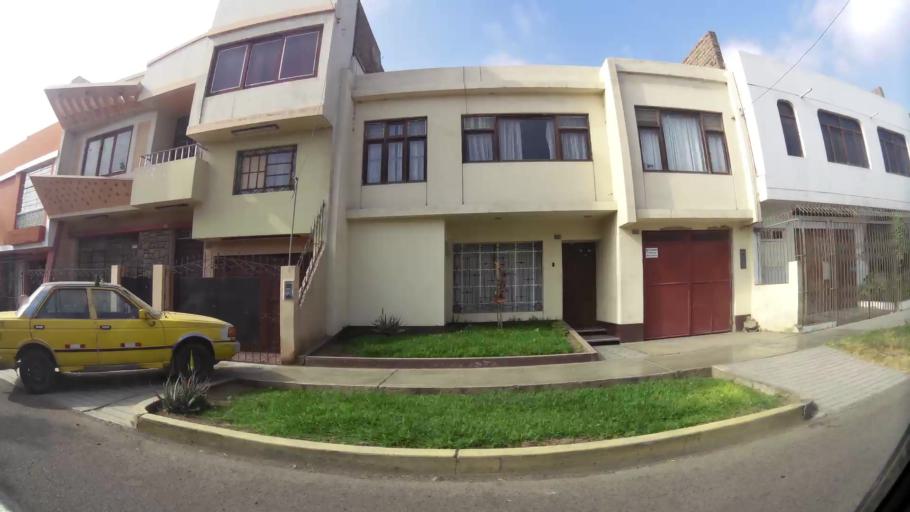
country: PE
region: La Libertad
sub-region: Provincia de Trujillo
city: Trujillo
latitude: -8.1108
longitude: -79.0153
